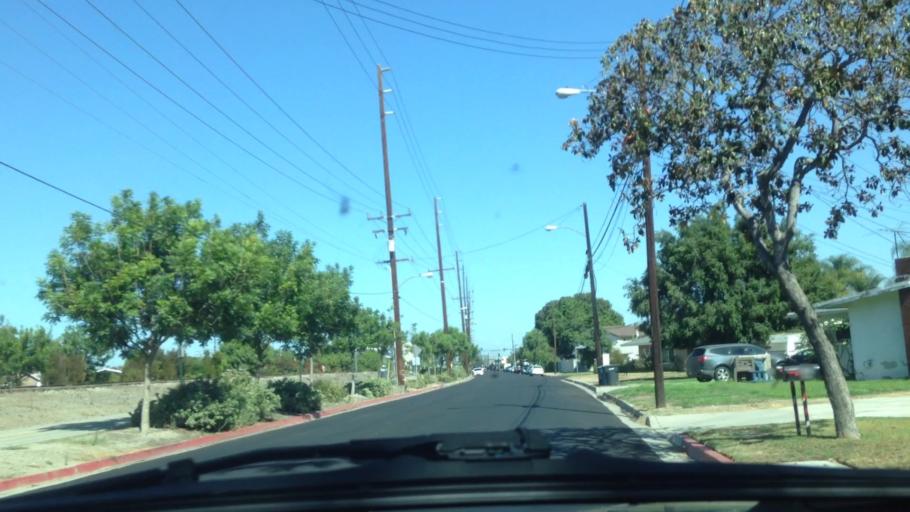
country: US
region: California
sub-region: Los Angeles County
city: Bellflower
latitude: 33.8803
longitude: -118.1142
